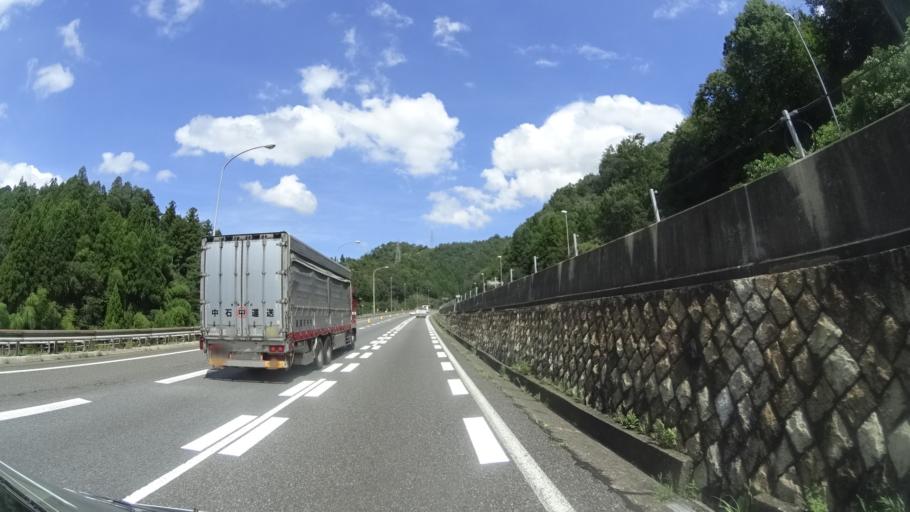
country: JP
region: Shiga Prefecture
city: Hikone
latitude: 35.2925
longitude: 136.2981
